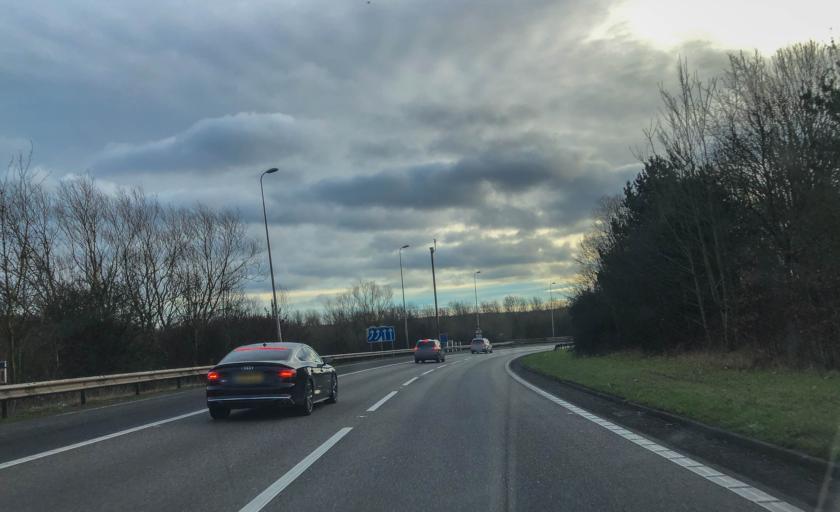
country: GB
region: England
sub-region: Kent
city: Halstead
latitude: 51.2957
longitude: 0.1475
